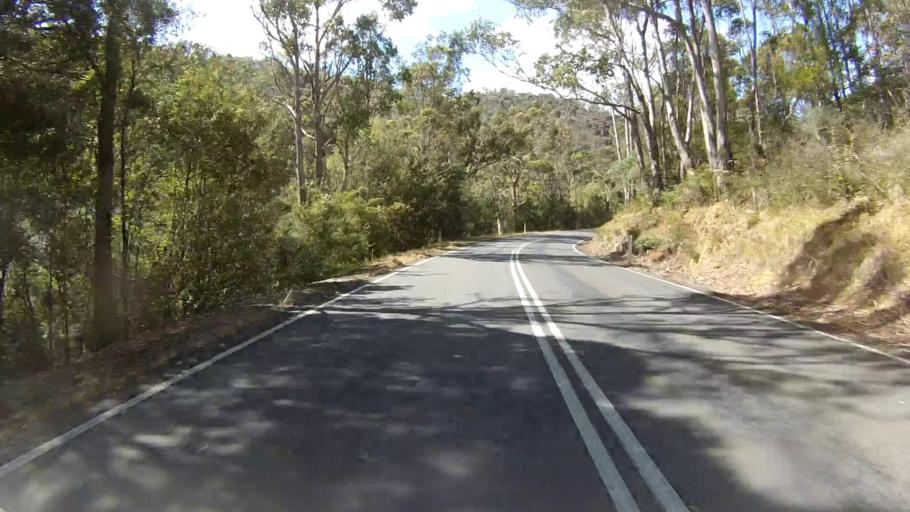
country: AU
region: Tasmania
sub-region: Derwent Valley
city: New Norfolk
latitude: -42.6774
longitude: 146.7629
